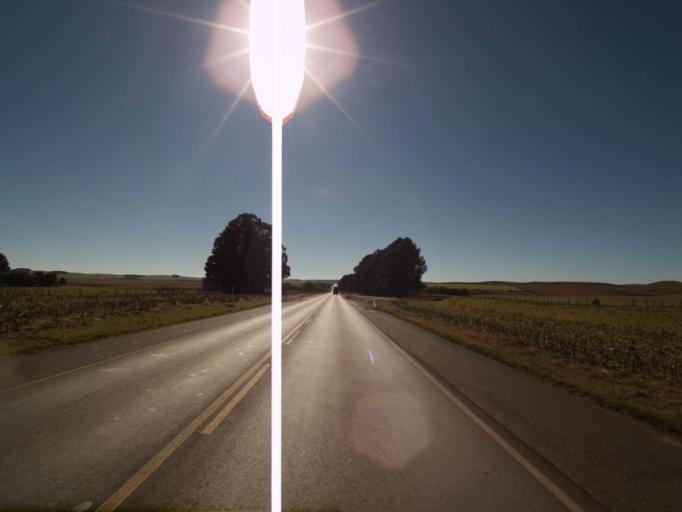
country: BR
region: Parana
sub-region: Palmas
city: Palmas
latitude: -26.7778
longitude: -51.6830
